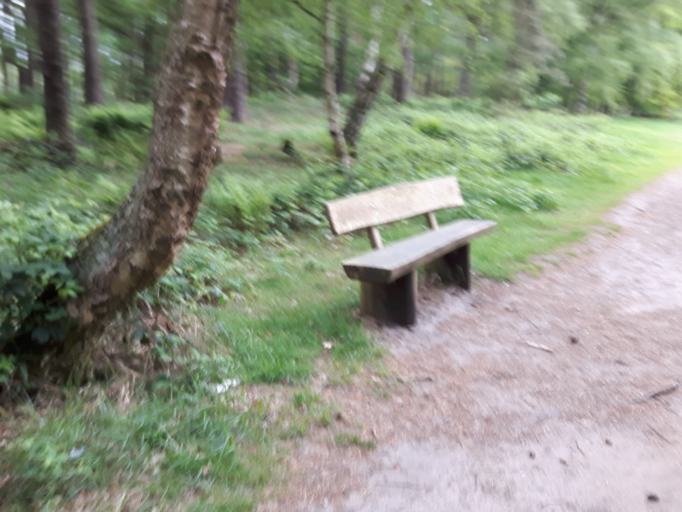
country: DE
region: North Rhine-Westphalia
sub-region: Regierungsbezirk Munster
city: Haltern
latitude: 51.7317
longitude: 7.2394
